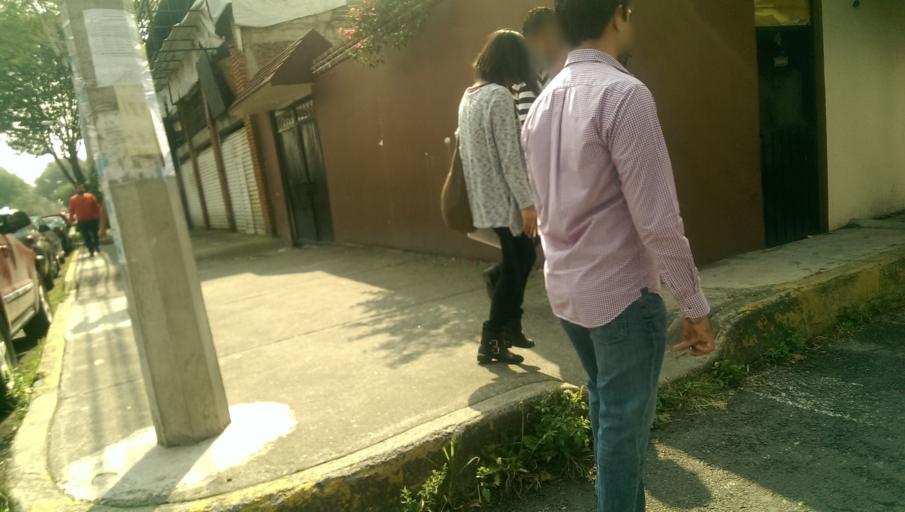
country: MX
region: Mexico City
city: Tlalpan
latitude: 19.2855
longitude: -99.1326
